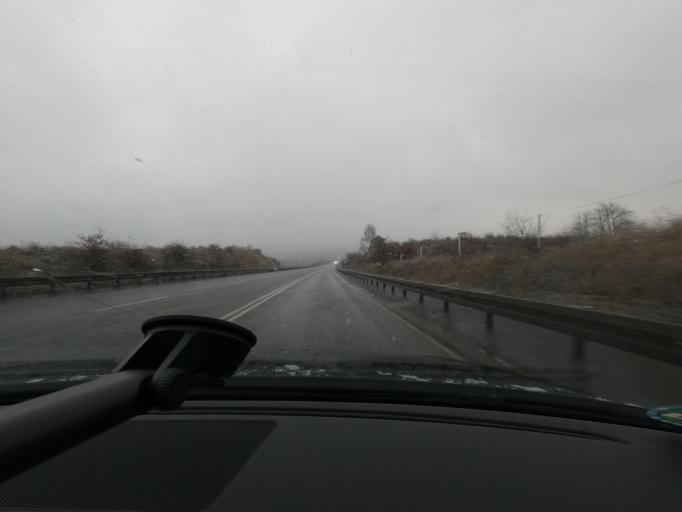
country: DE
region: Thuringia
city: Dingelstadt
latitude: 51.3229
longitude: 10.3289
